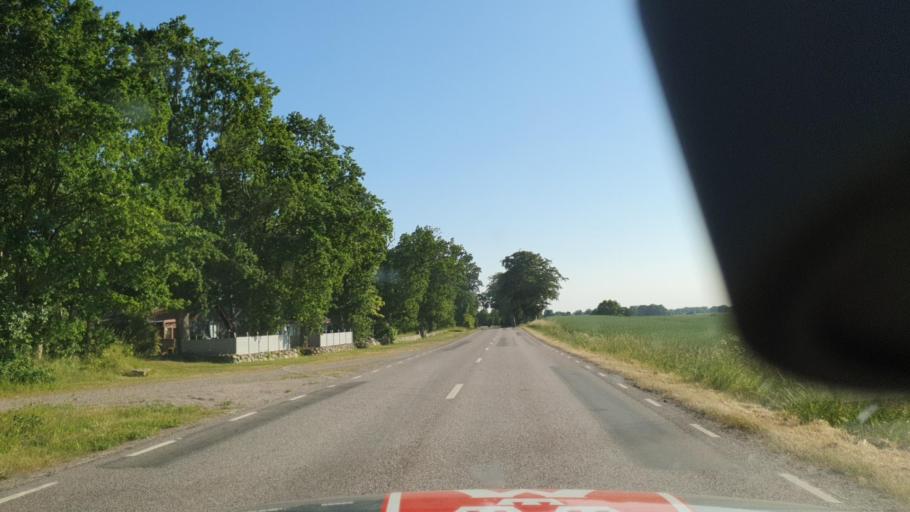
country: SE
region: Kalmar
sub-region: Kalmar Kommun
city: Ljungbyholm
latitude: 56.5265
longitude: 16.1718
